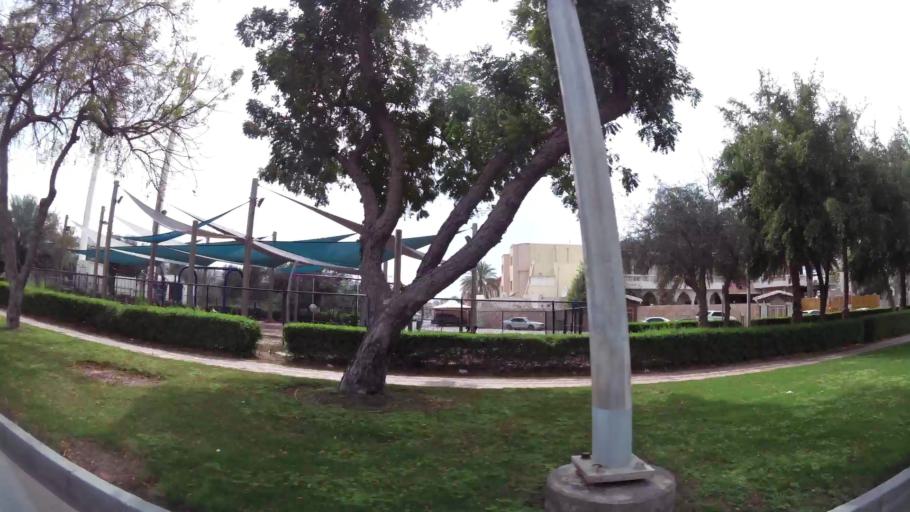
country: AE
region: Abu Dhabi
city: Abu Dhabi
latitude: 24.4664
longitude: 54.3654
